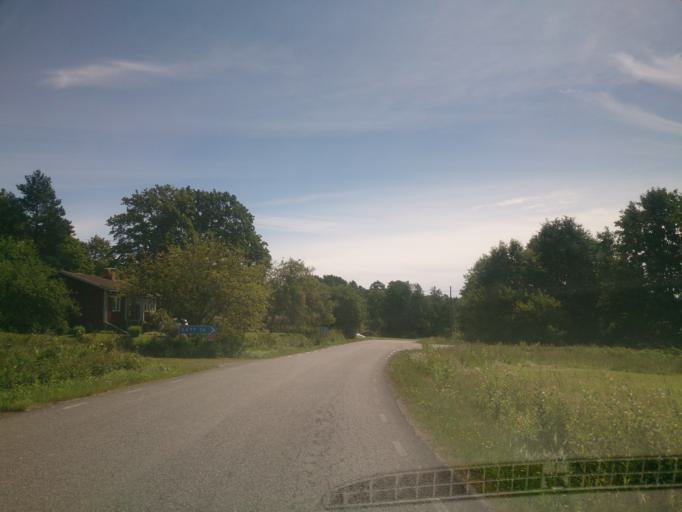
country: SE
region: OEstergoetland
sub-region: Valdemarsviks Kommun
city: Valdemarsvik
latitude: 58.2780
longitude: 16.6927
